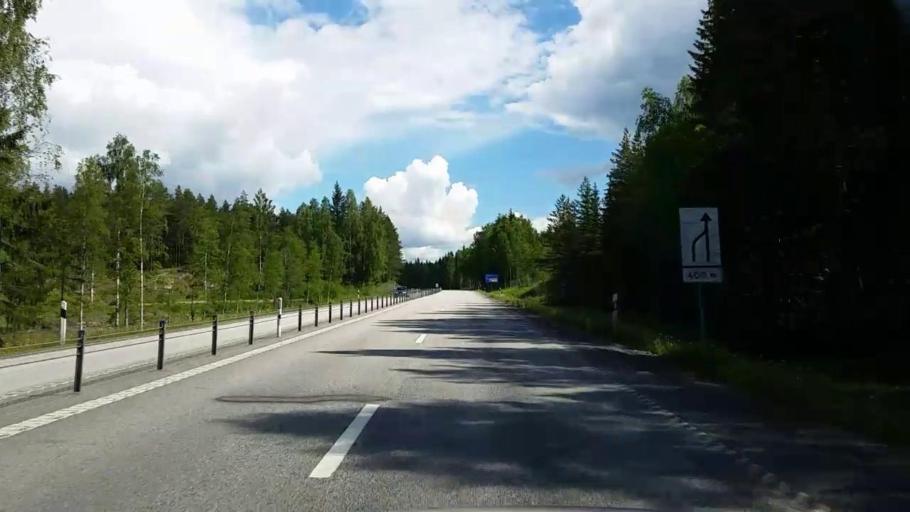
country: SE
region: Vaestmanland
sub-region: Fagersta Kommun
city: Fagersta
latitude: 60.0193
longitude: 15.7886
